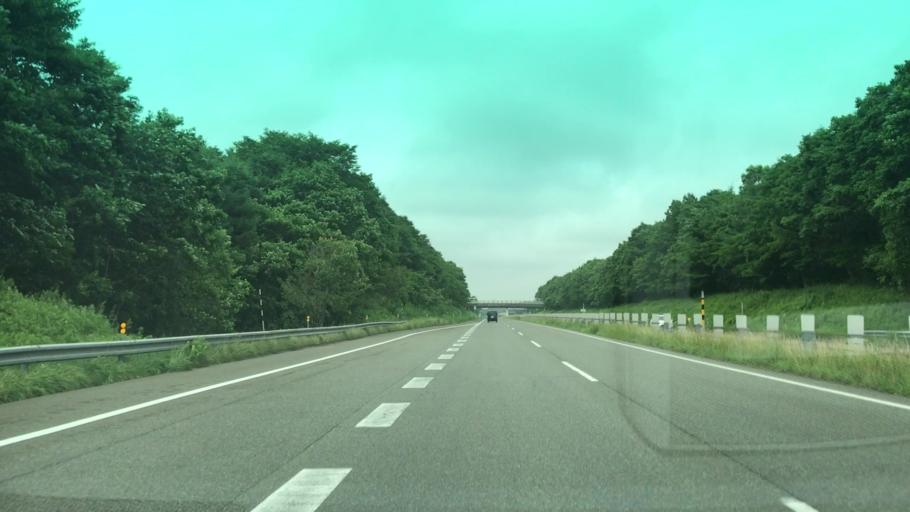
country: JP
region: Hokkaido
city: Tomakomai
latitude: 42.7136
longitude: 141.6522
